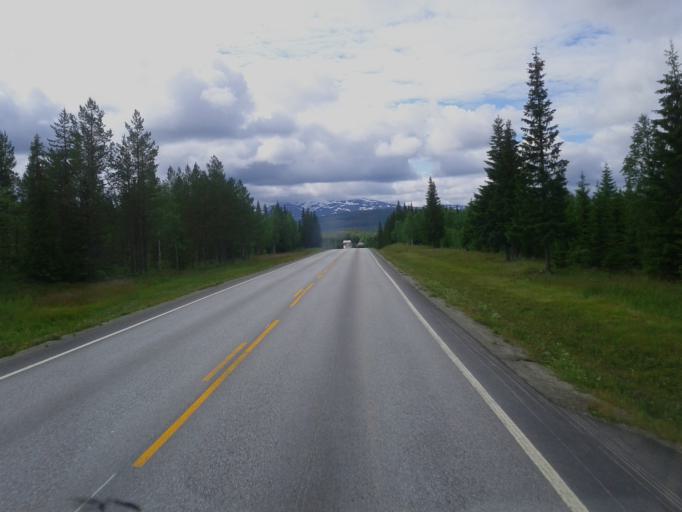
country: NO
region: Nord-Trondelag
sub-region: Namsskogan
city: Namsskogan
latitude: 64.7199
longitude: 12.8006
